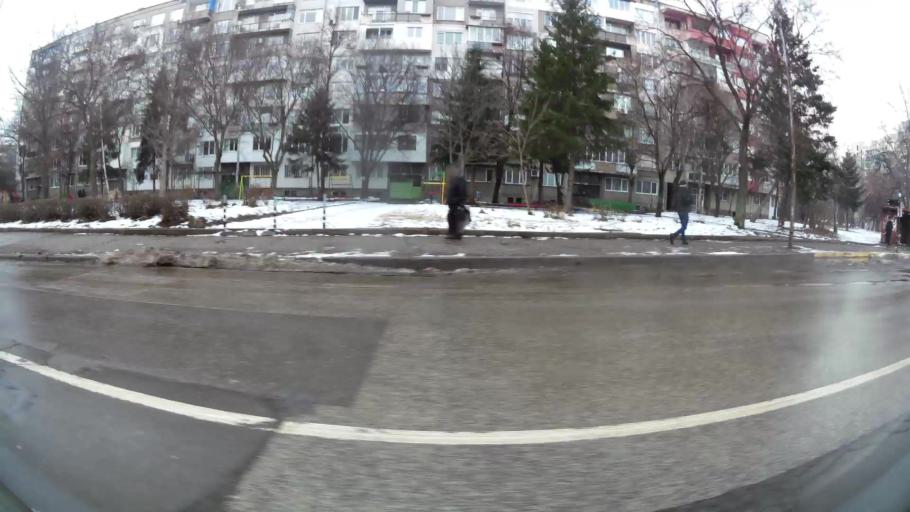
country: BG
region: Sofia-Capital
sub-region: Stolichna Obshtina
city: Sofia
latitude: 42.7030
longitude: 23.2858
